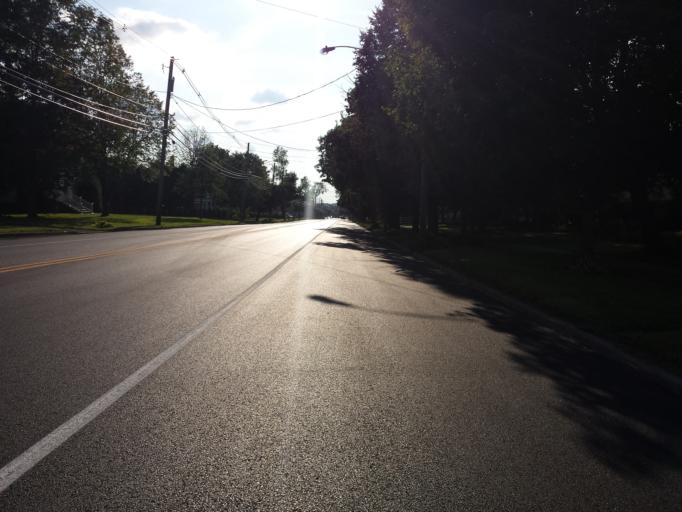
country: US
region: New York
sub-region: St. Lawrence County
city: Potsdam
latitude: 44.6699
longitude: -74.9771
